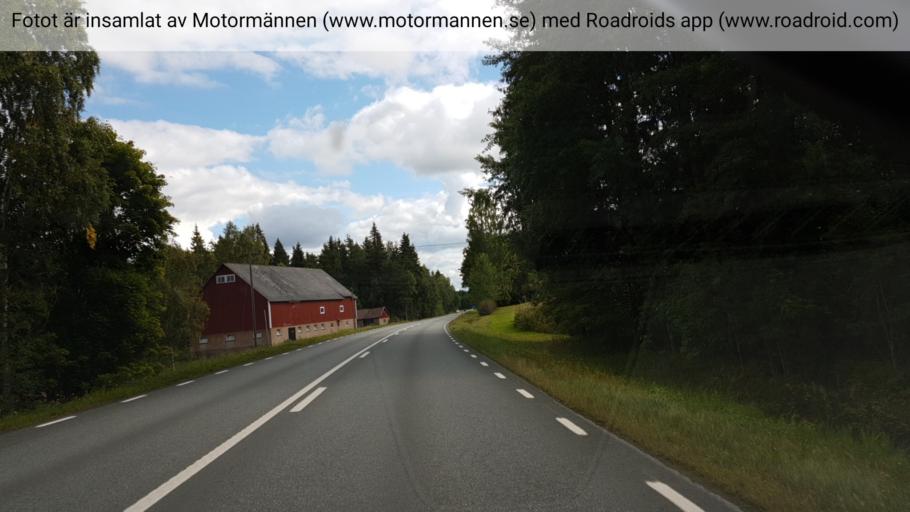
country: SE
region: Joenkoeping
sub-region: Jonkopings Kommun
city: Tenhult
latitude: 57.7774
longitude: 14.4440
